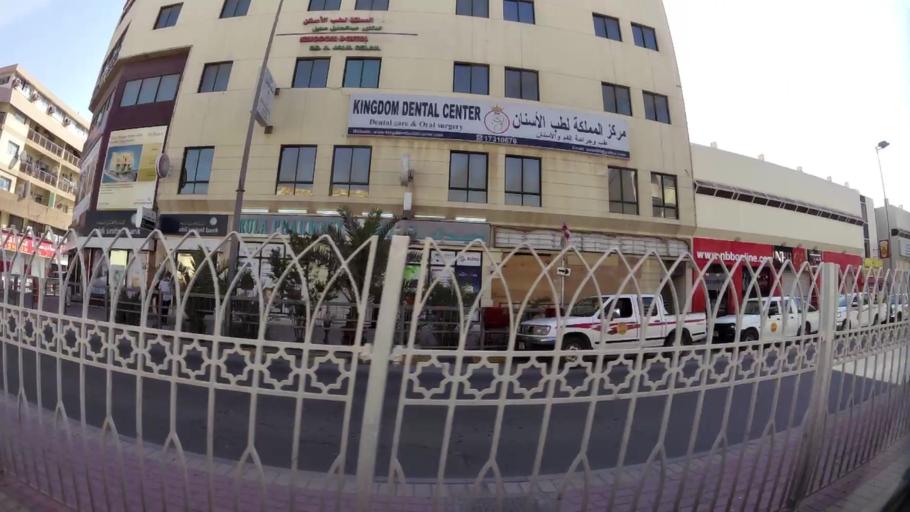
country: BH
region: Manama
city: Manama
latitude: 26.2275
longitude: 50.5880
